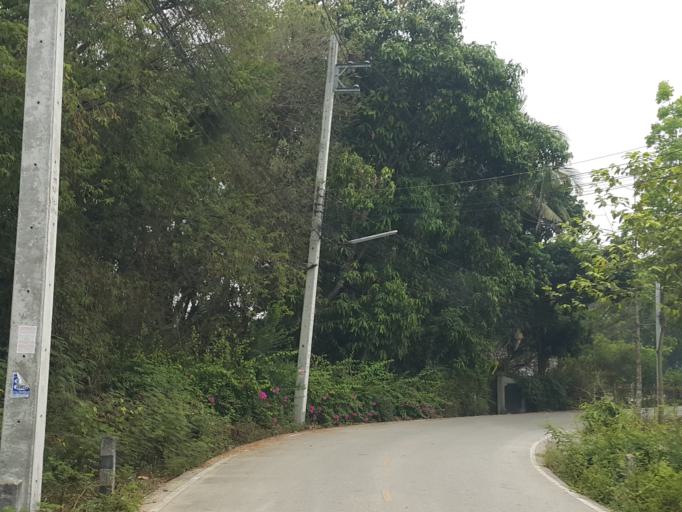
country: TH
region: Chiang Mai
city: Saraphi
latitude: 18.7257
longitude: 99.0077
